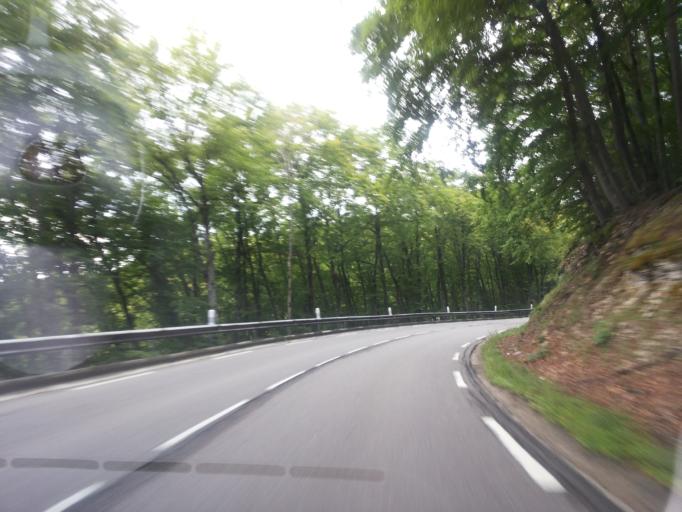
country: FR
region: Lorraine
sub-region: Departement des Vosges
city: Neufchateau
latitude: 48.3517
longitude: 5.7154
